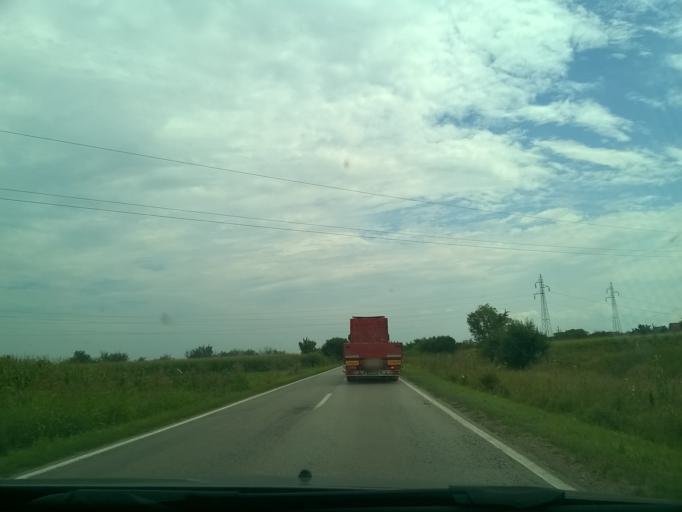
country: RS
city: Klek
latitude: 45.3835
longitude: 20.4437
